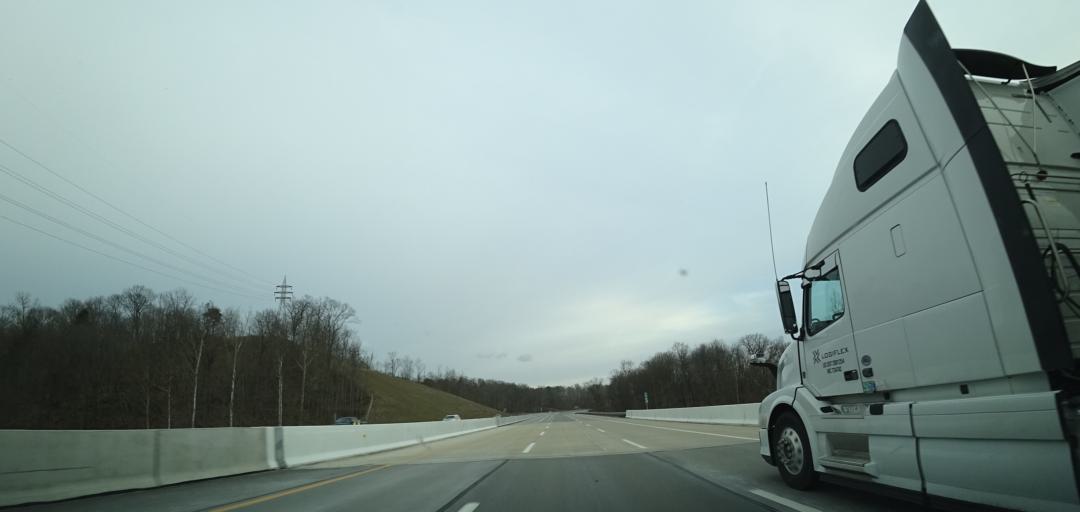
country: US
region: Pennsylvania
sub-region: Allegheny County
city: Oakmont
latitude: 40.5518
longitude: -79.8310
